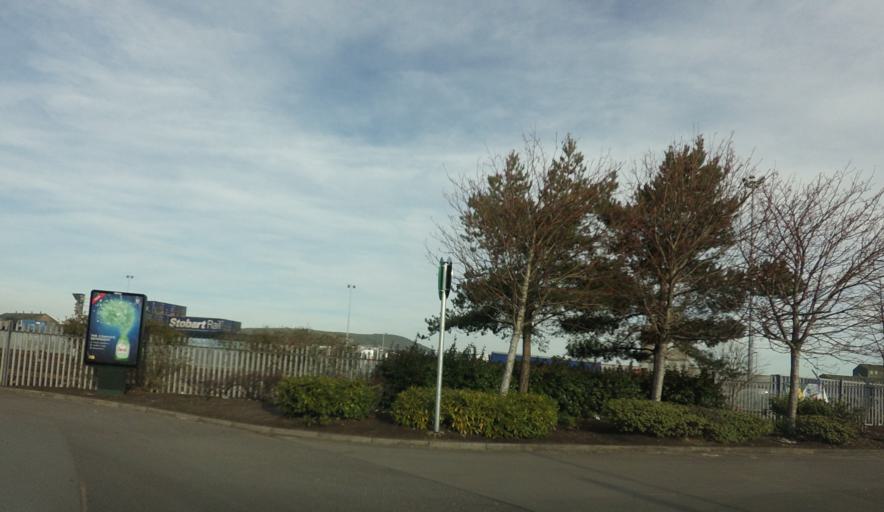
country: GB
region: Scotland
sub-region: Highland
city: Inverness
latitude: 57.4816
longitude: -4.2175
